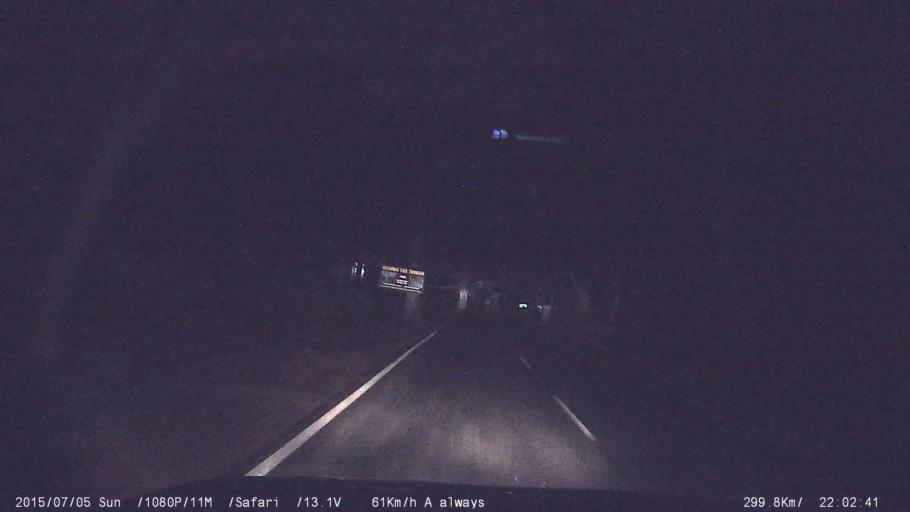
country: IN
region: Kerala
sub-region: Palakkad district
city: Mannarakkat
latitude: 10.9367
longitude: 76.5264
